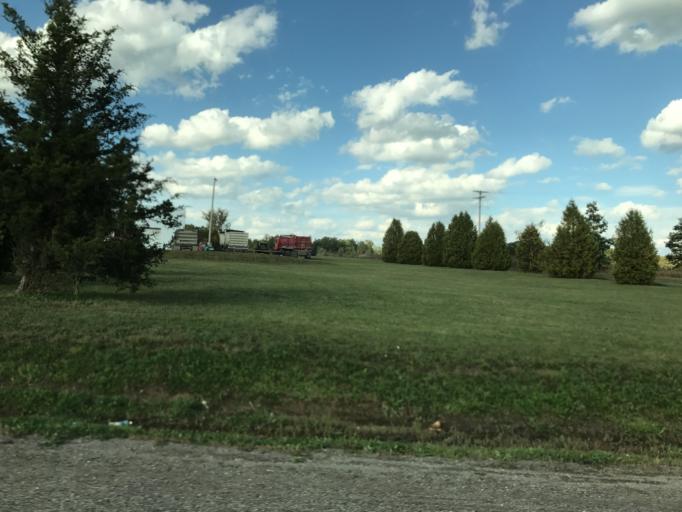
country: US
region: Michigan
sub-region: Oakland County
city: Wixom
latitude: 42.5064
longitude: -83.5910
